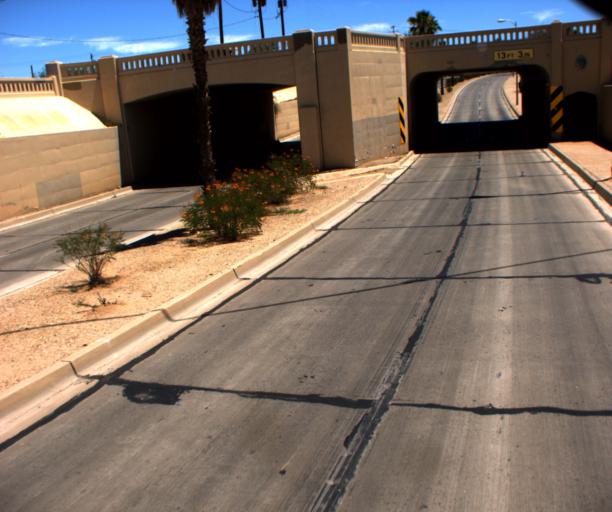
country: US
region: Arizona
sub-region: Pinal County
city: Casa Grande
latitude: 32.8797
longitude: -111.7624
